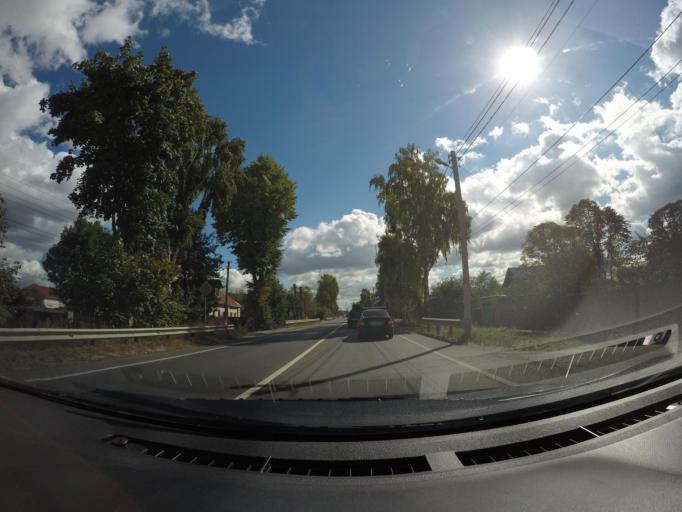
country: RU
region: Moskovskaya
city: Rechitsy
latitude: 55.5957
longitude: 38.4808
